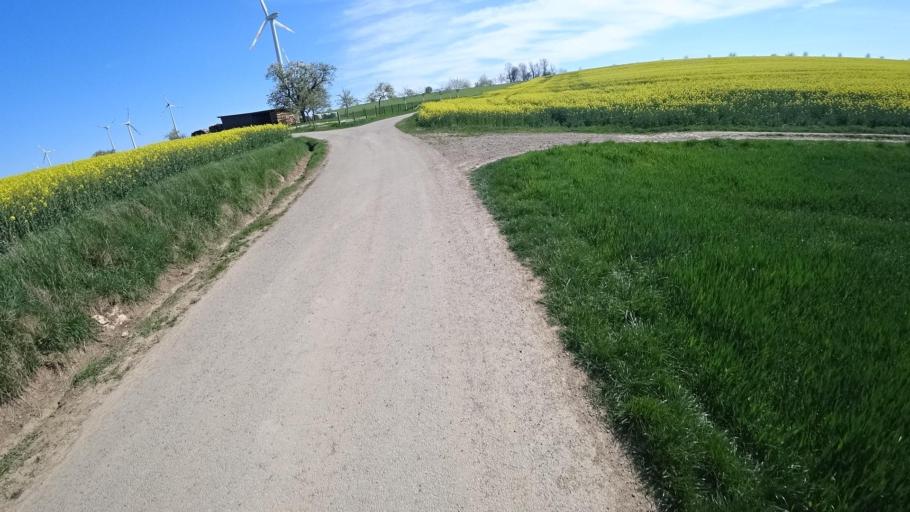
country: DE
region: Rheinland-Pfalz
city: Eisenach
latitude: 49.8465
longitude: 6.5160
